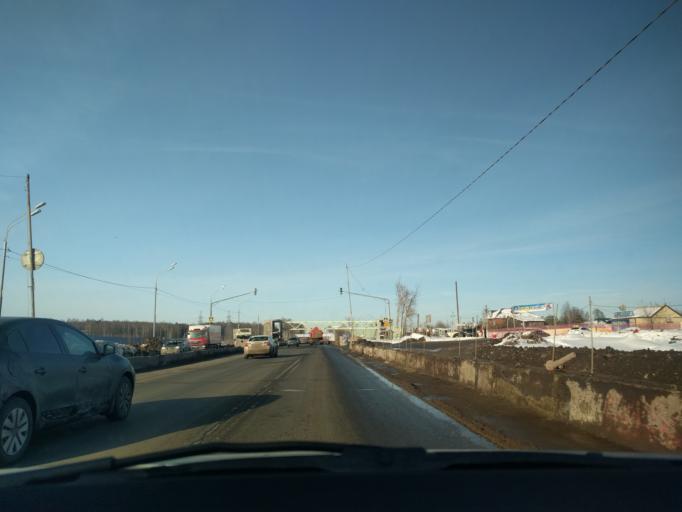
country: RU
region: Moskovskaya
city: Sheremet'yevskiy
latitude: 55.9972
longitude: 37.5359
